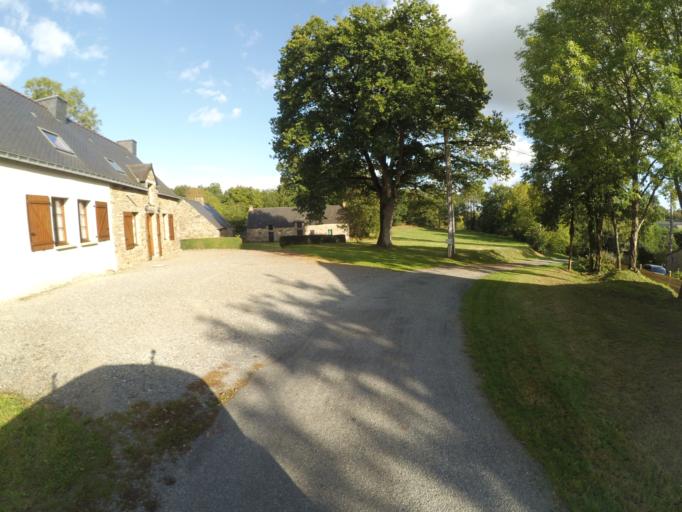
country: FR
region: Brittany
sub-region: Departement du Morbihan
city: Peillac
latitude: 47.7226
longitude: -2.2024
